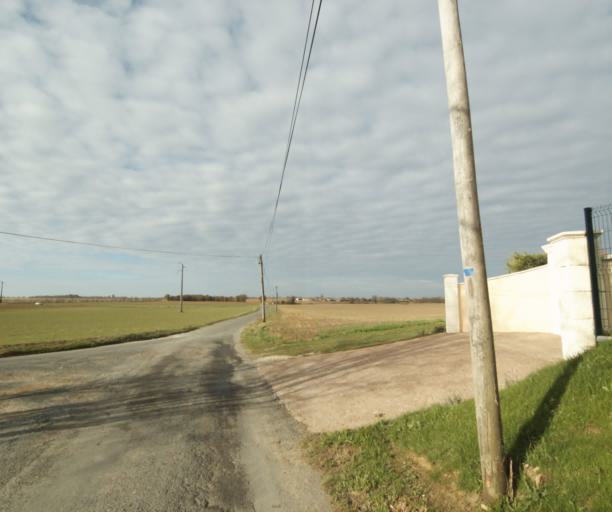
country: FR
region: Poitou-Charentes
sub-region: Departement de la Charente-Maritime
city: Corme-Royal
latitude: 45.7315
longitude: -0.8142
